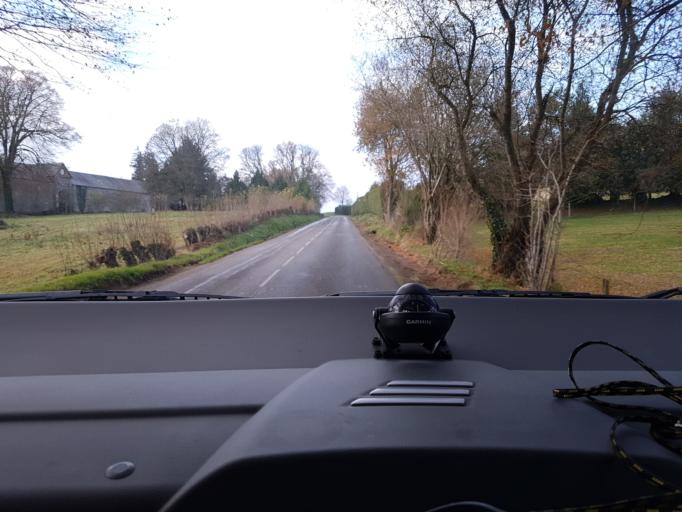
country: FR
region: Lower Normandy
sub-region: Departement du Calvados
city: Saint-Sever-Calvados
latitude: 48.7534
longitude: -1.0553
